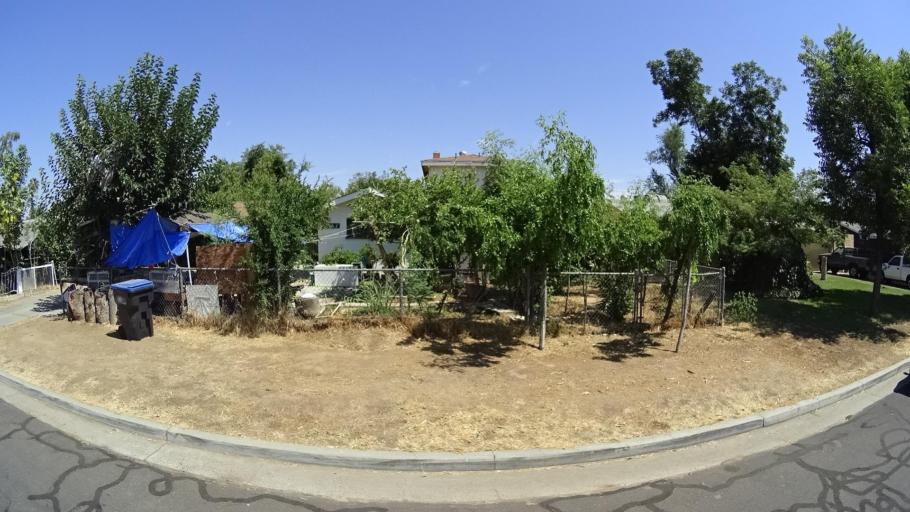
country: US
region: California
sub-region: Fresno County
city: Sunnyside
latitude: 36.7556
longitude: -119.7106
